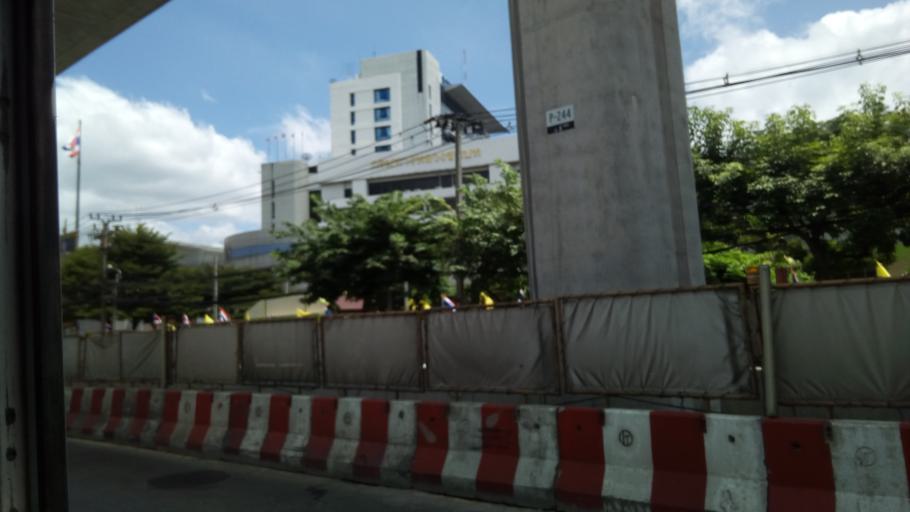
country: TH
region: Bangkok
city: Lak Si
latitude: 13.8621
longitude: 100.5888
